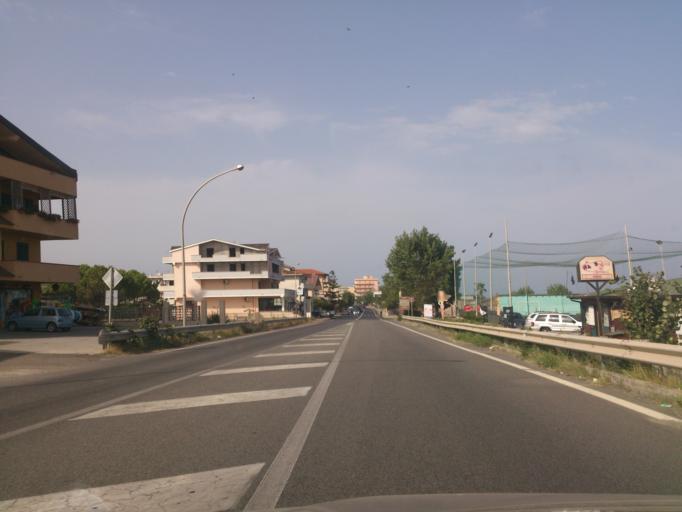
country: IT
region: Calabria
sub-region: Provincia di Reggio Calabria
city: Monasterace Marina
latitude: 38.4288
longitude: 16.5712
